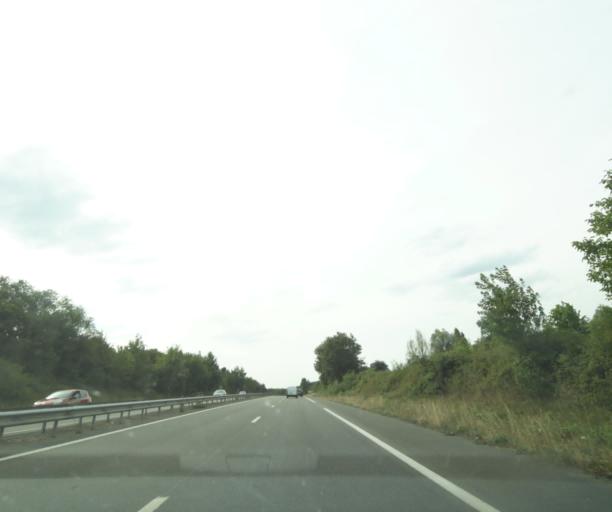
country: FR
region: Pays de la Loire
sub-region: Departement de la Sarthe
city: Coulaines
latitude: 48.0300
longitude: 0.2165
